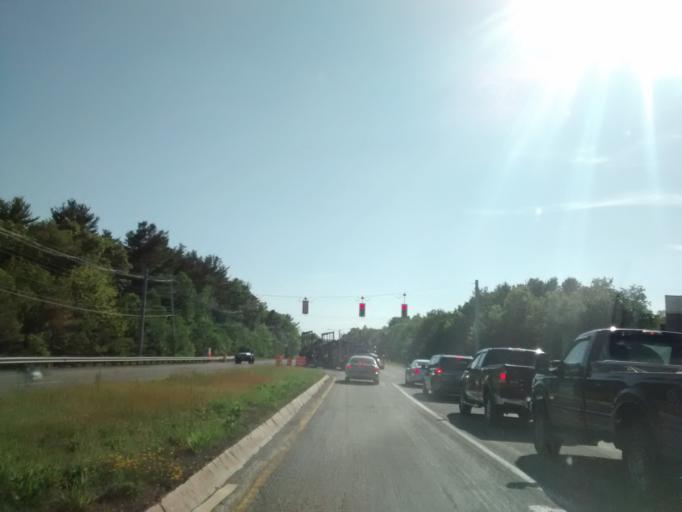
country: US
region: Massachusetts
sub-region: Worcester County
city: Sturbridge
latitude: 42.1282
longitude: -72.0489
